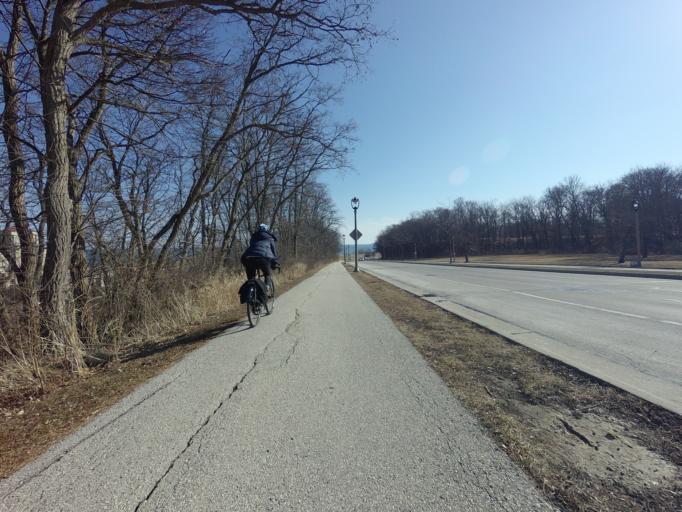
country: US
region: Wisconsin
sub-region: Milwaukee County
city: Shorewood
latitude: 43.0732
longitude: -87.8677
